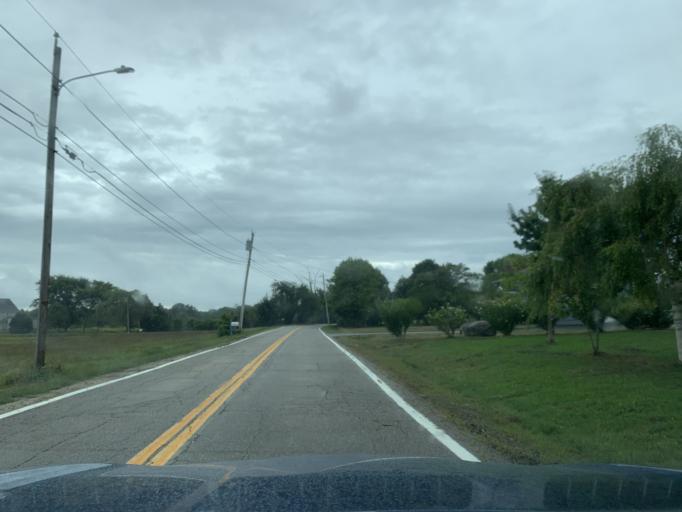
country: US
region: Rhode Island
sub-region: Bristol County
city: Warren
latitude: 41.7504
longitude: -71.2665
